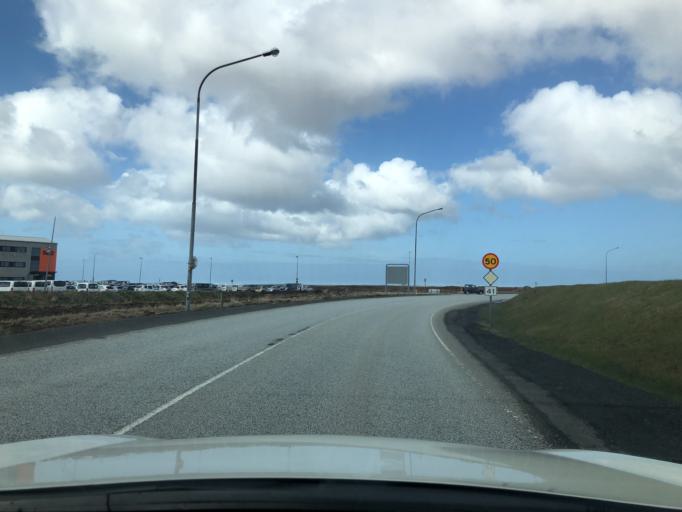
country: IS
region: Southern Peninsula
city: Reykjanesbaer
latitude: 63.9984
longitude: -22.6274
